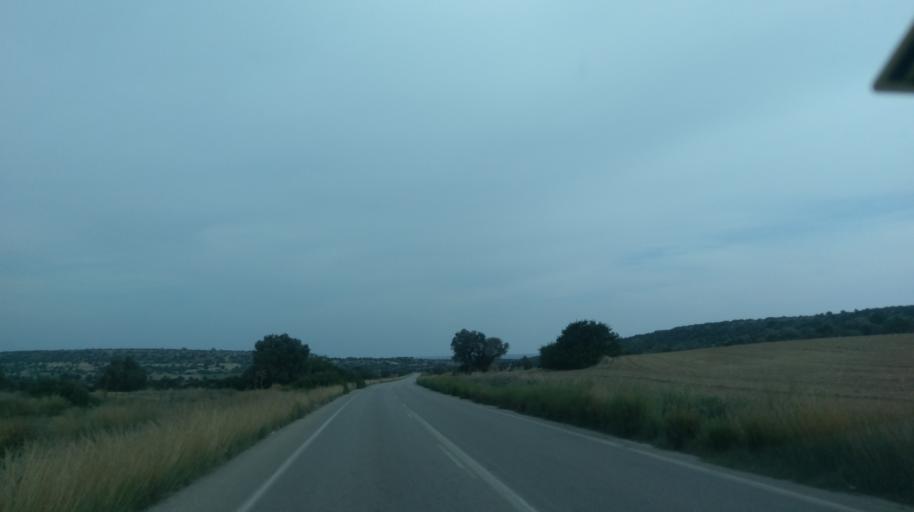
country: CY
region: Ammochostos
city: Leonarisso
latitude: 35.4018
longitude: 34.0868
